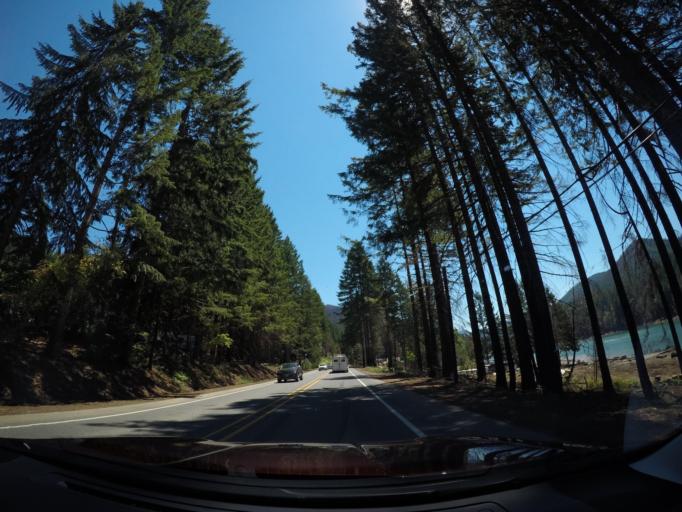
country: US
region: Oregon
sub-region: Linn County
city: Mill City
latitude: 44.7290
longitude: -122.1433
